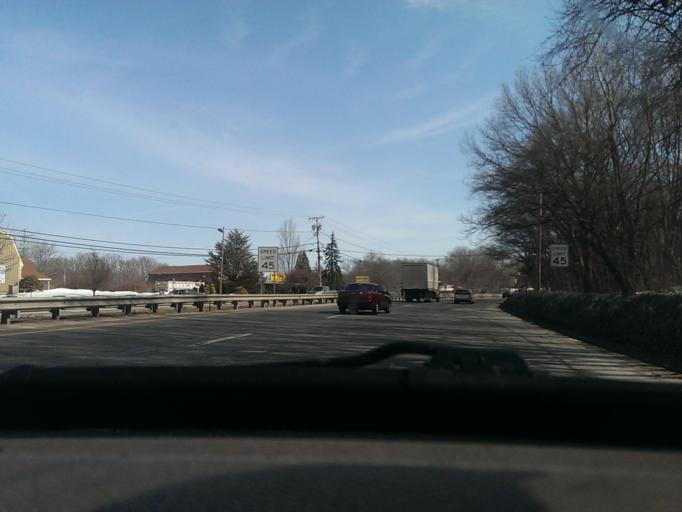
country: US
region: Rhode Island
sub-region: Providence County
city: Woonsocket
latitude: 41.9674
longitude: -71.5040
